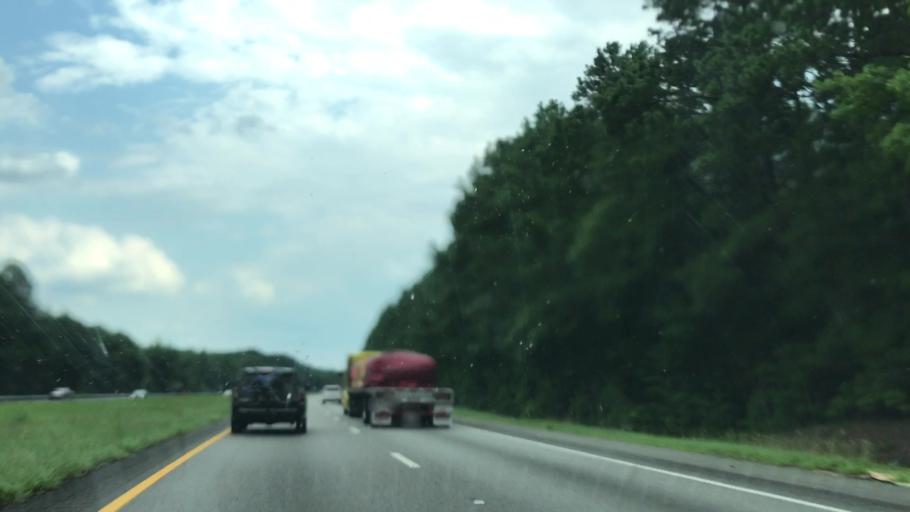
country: US
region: South Carolina
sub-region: Richland County
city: Blythewood
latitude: 34.3003
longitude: -80.9976
